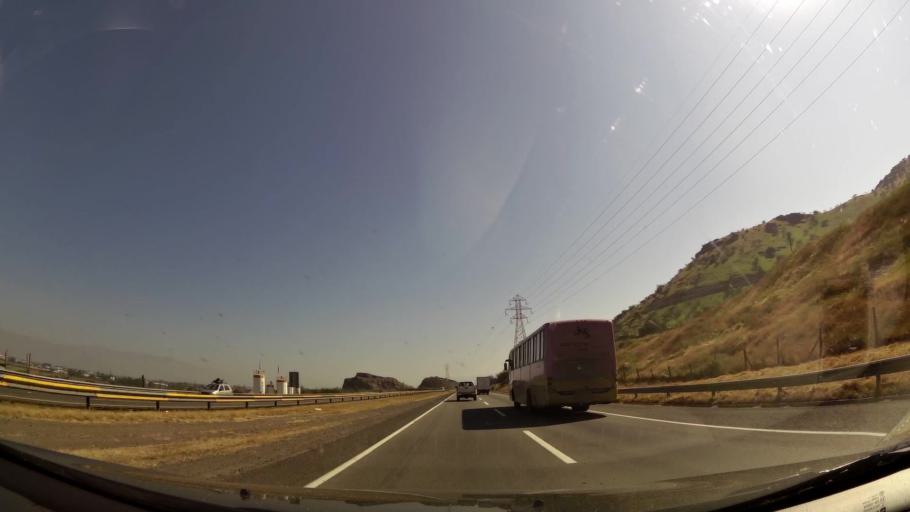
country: CL
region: Santiago Metropolitan
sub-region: Provincia de Chacabuco
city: Chicureo Abajo
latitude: -33.3221
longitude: -70.7059
